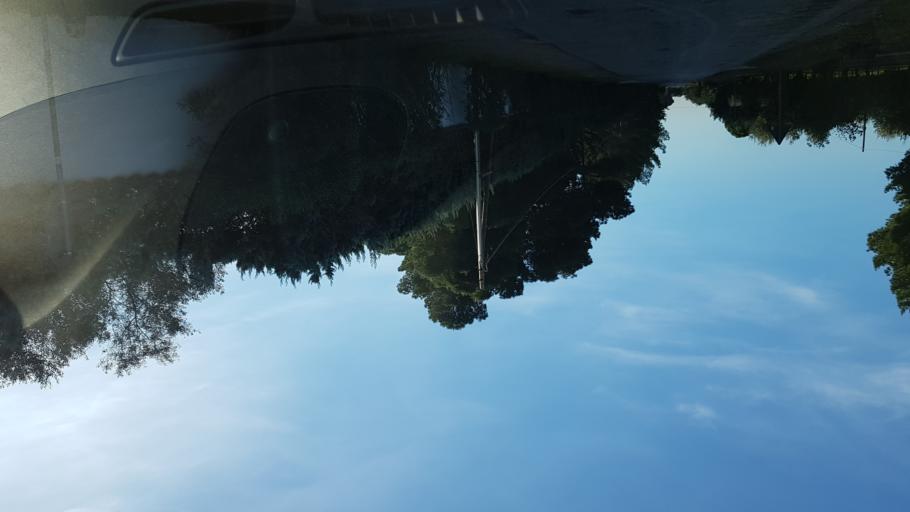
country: IT
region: Apulia
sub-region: Provincia di Brindisi
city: San Vito dei Normanni
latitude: 40.6759
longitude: 17.7761
